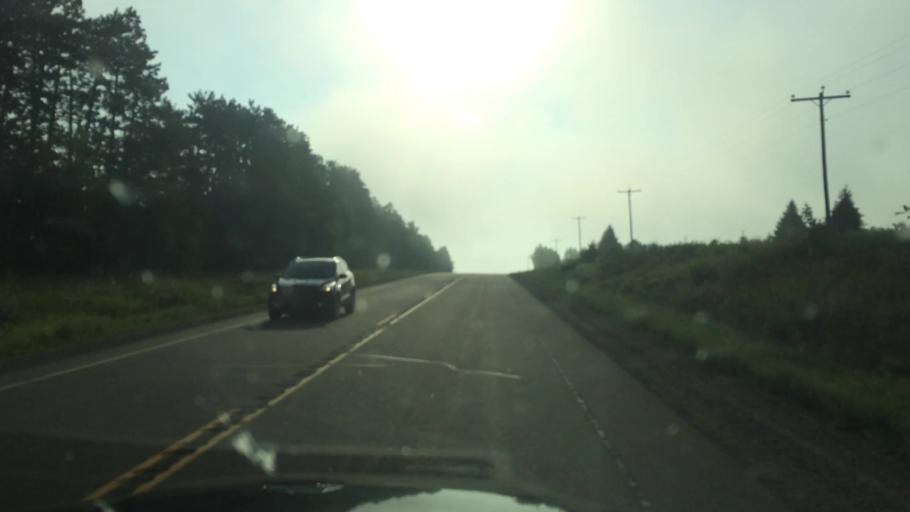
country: US
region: Wisconsin
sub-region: Lincoln County
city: Merrill
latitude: 45.1779
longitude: -89.5840
